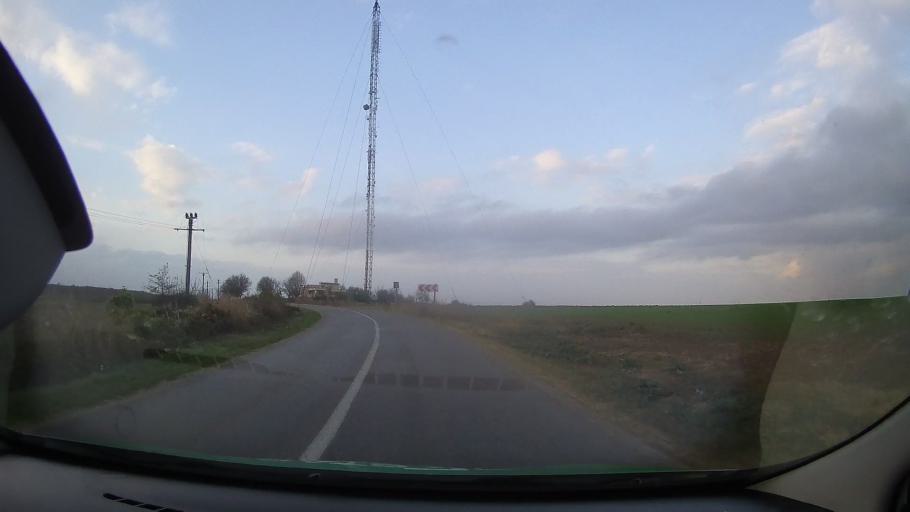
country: RO
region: Constanta
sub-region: Comuna Dobromir
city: Dobromir
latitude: 44.0481
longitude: 27.7534
